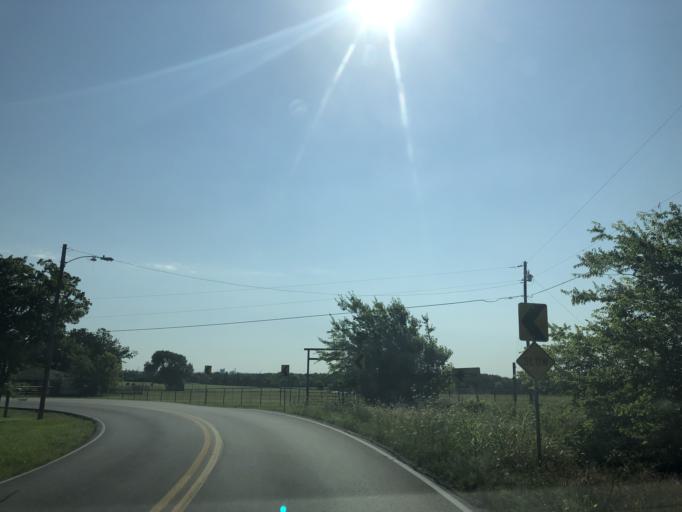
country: US
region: Texas
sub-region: Dallas County
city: Sunnyvale
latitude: 32.8228
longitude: -96.5877
